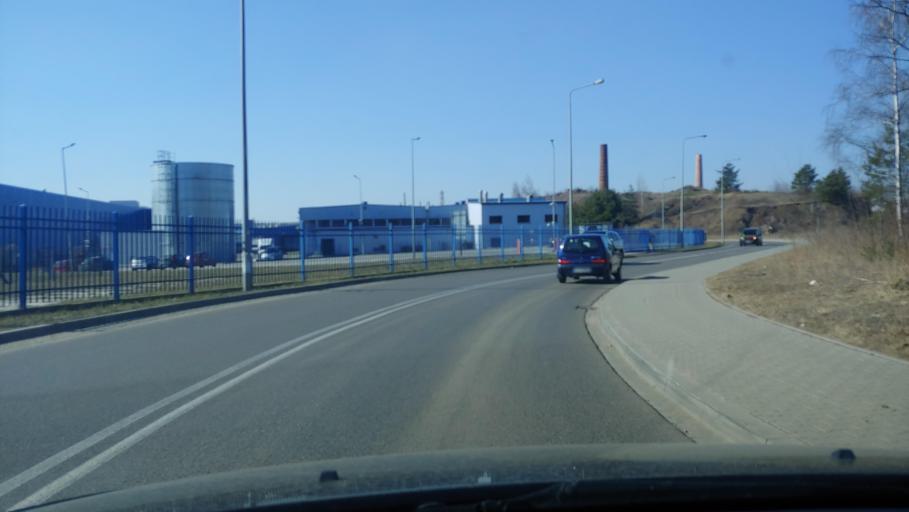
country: PL
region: Lesser Poland Voivodeship
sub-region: Powiat chrzanowski
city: Trzebinia
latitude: 50.1524
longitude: 19.4654
